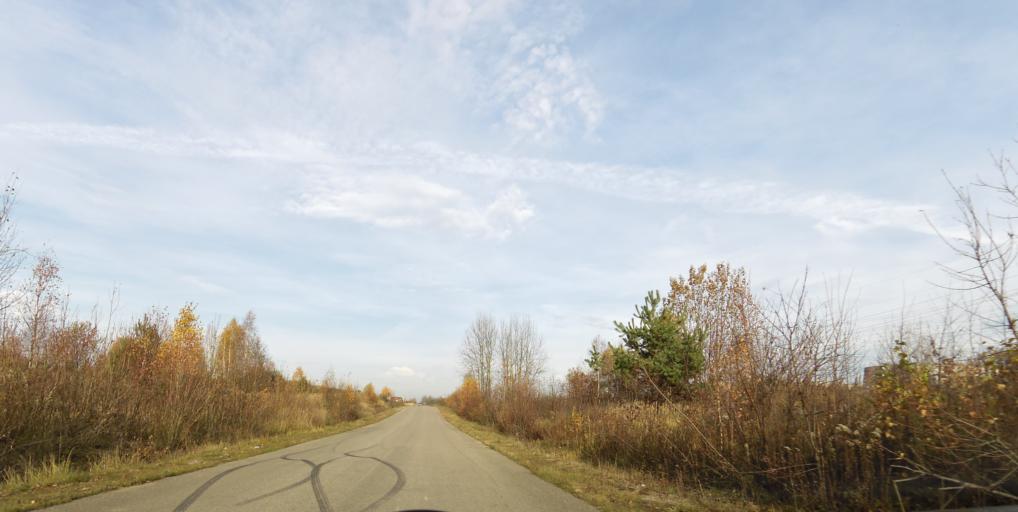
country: LT
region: Vilnius County
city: Justiniskes
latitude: 54.7088
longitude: 25.2061
